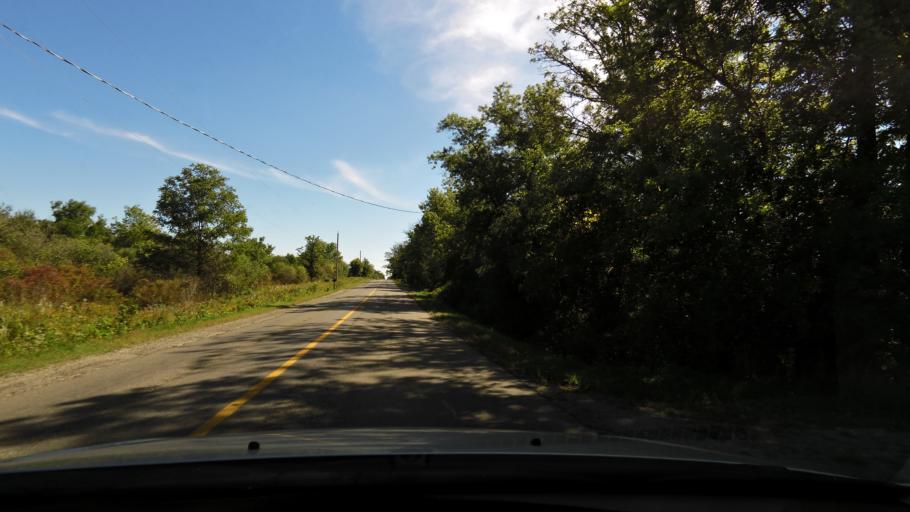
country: CA
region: Ontario
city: Ancaster
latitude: 43.0713
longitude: -80.0689
